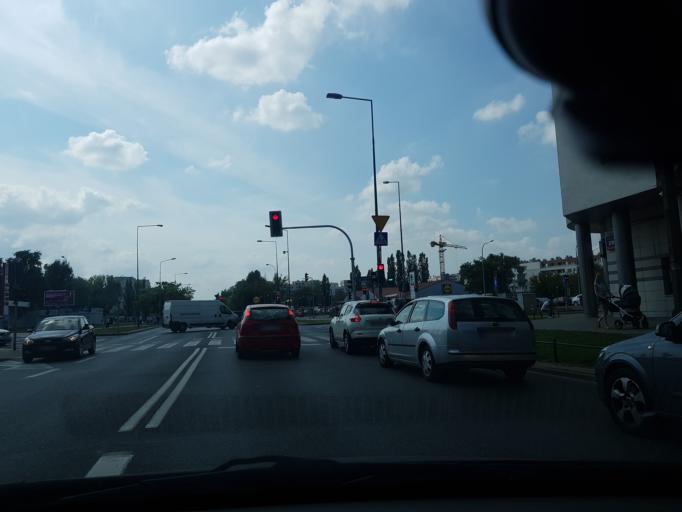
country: PL
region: Masovian Voivodeship
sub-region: Warszawa
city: Bielany
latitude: 52.2892
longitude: 20.9343
